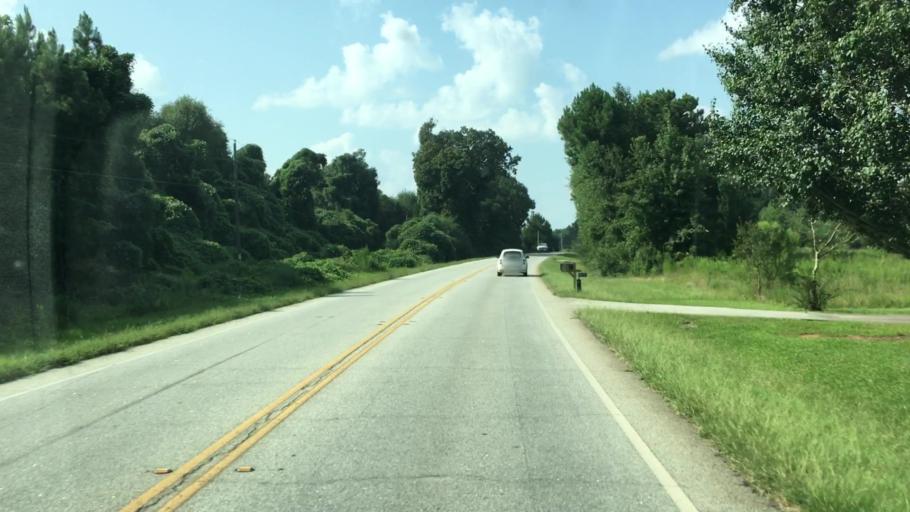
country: US
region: Georgia
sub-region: Walton County
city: Social Circle
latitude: 33.5841
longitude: -83.7469
